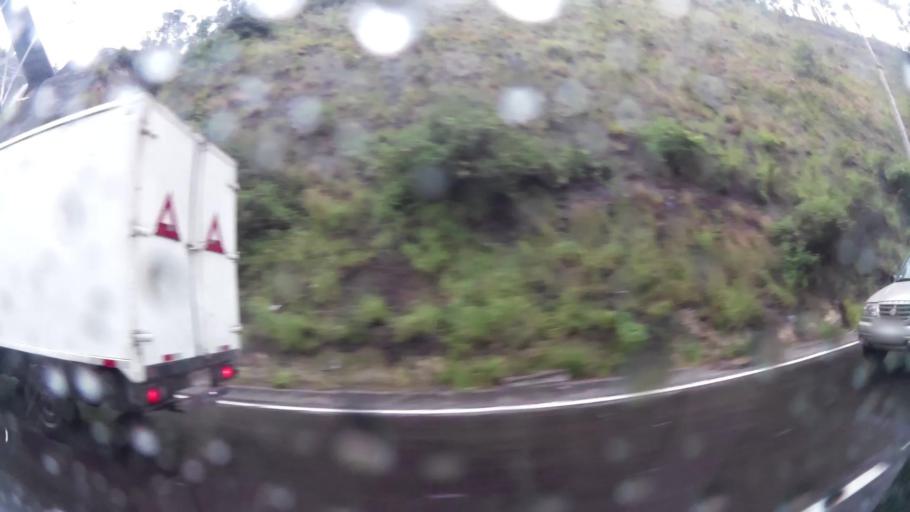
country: EC
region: Pichincha
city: Quito
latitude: -0.1458
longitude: -78.4457
